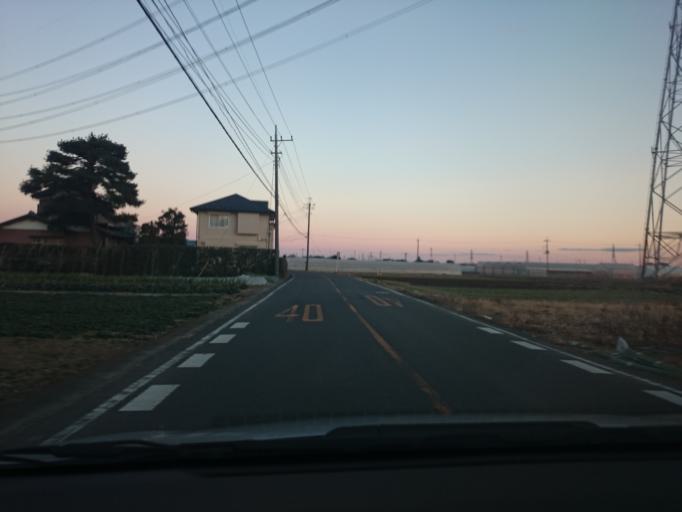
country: JP
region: Gunma
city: Sakai-nakajima
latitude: 36.2383
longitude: 139.2404
